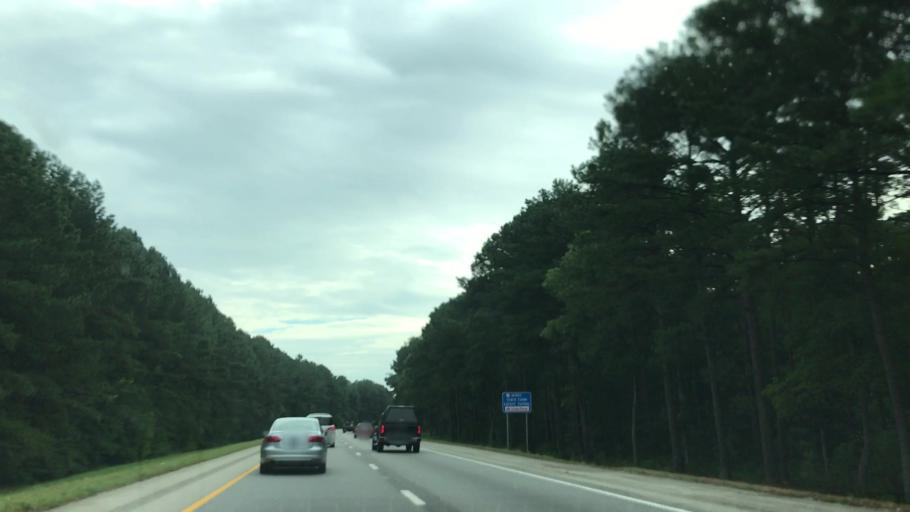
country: US
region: North Carolina
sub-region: Wilson County
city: Lucama
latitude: 35.7141
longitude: -78.0380
